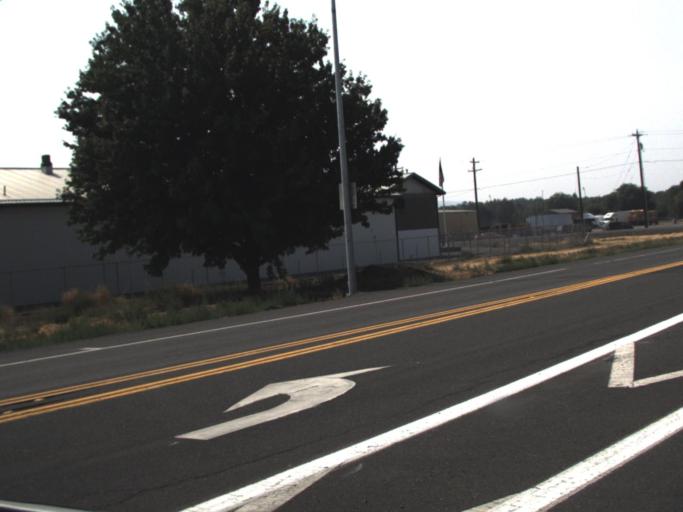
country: US
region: Washington
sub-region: Yakima County
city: Terrace Heights
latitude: 46.5771
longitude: -120.4494
